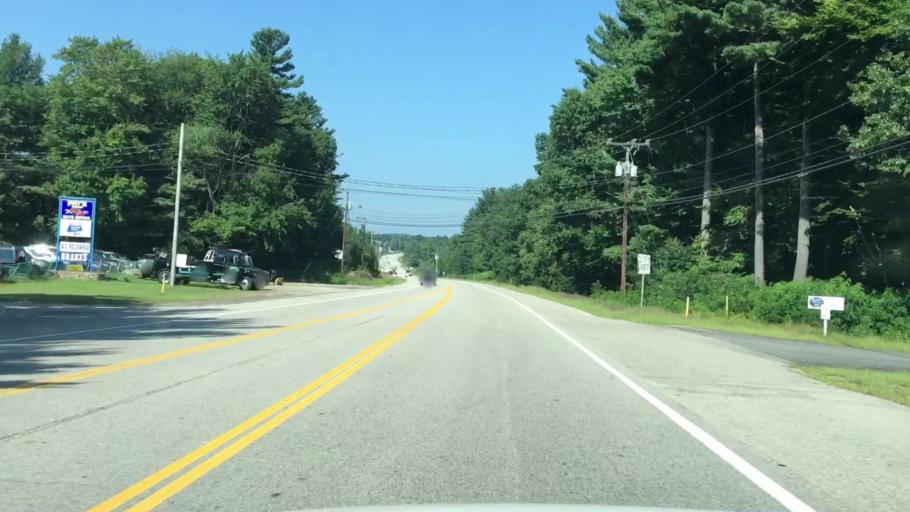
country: US
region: New Hampshire
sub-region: Rockingham County
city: Seabrook
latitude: 42.8972
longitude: -70.8879
